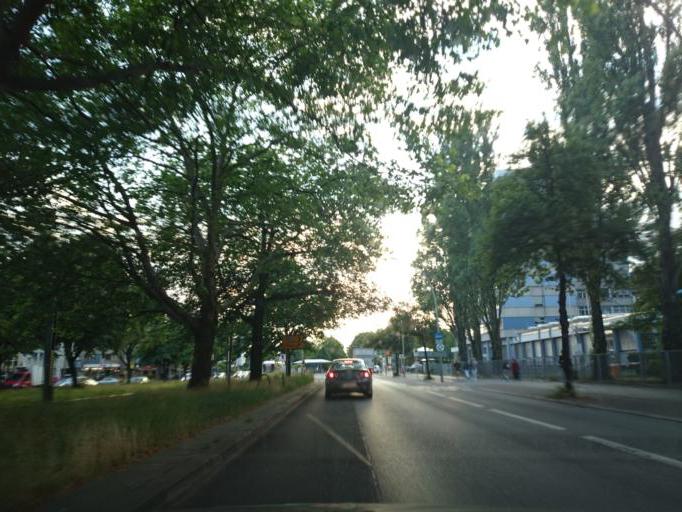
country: DE
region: Berlin
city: Gesundbrunnen
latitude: 52.5567
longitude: 13.3756
